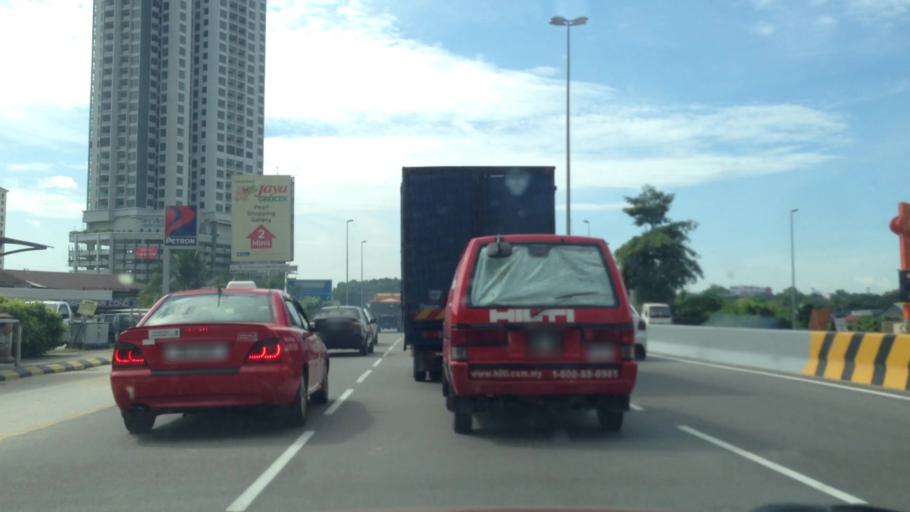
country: MY
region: Selangor
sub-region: Petaling
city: Petaling Jaya
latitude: 3.0832
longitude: 101.6630
